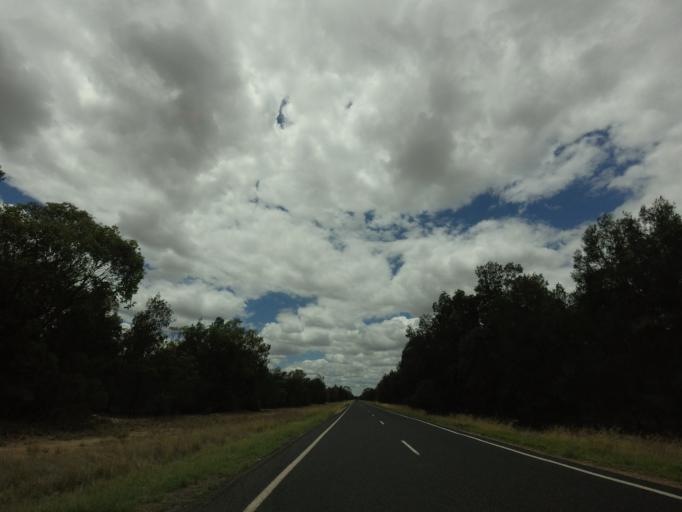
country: AU
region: Queensland
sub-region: Goondiwindi
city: Goondiwindi
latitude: -28.1635
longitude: 150.6158
